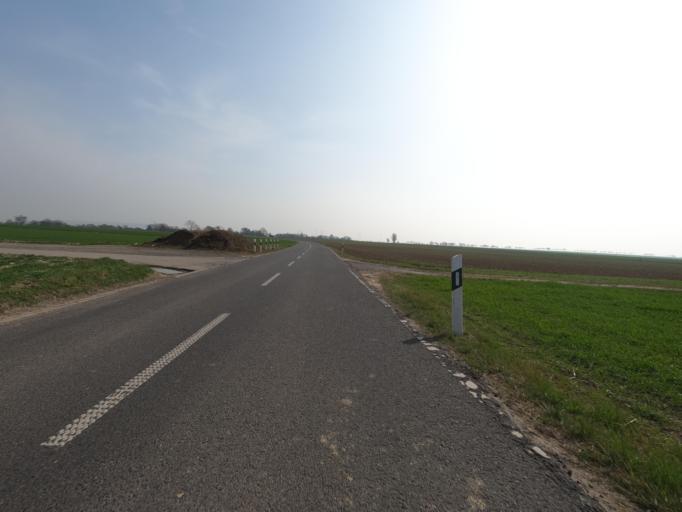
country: DE
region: North Rhine-Westphalia
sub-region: Regierungsbezirk Koln
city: Linnich
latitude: 51.0073
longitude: 6.3394
